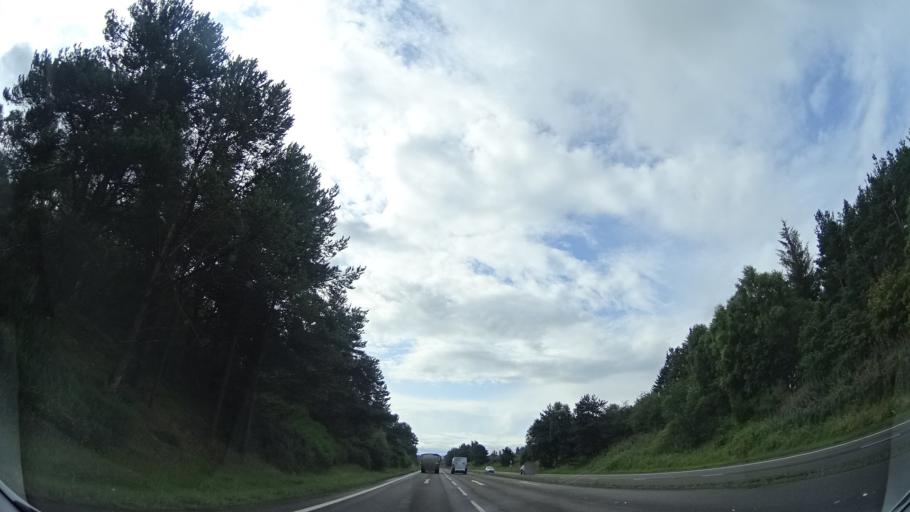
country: GB
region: Scotland
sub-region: Highland
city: Conon Bridge
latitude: 57.5319
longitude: -4.3274
